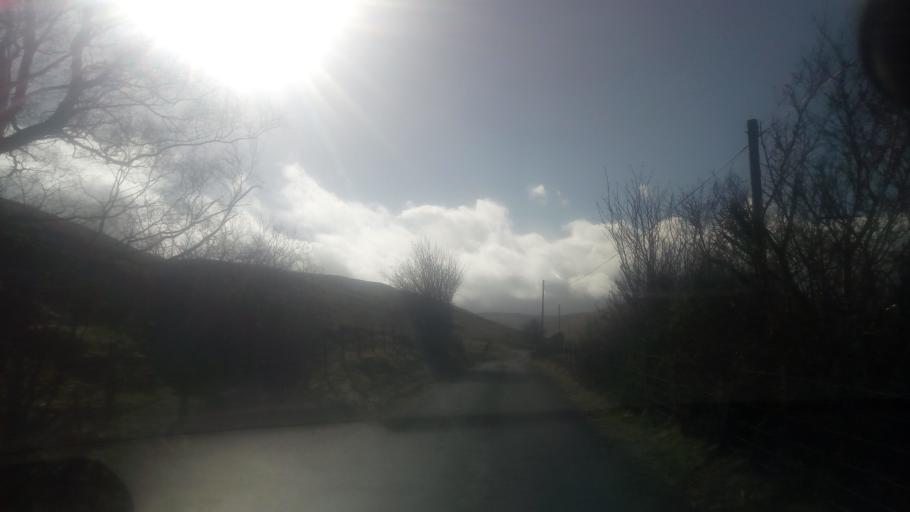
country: GB
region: Scotland
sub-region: The Scottish Borders
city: Innerleithen
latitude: 55.5084
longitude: -3.1024
